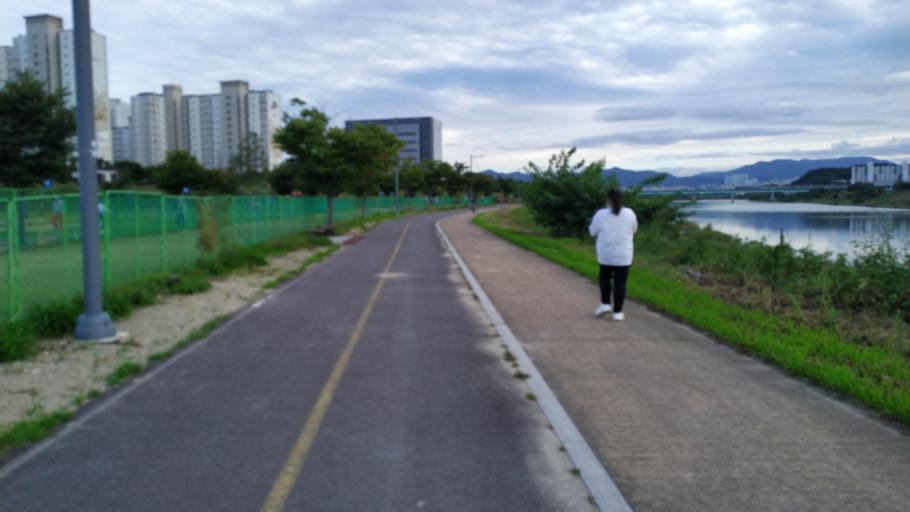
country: KR
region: Daegu
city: Daegu
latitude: 35.9267
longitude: 128.6320
